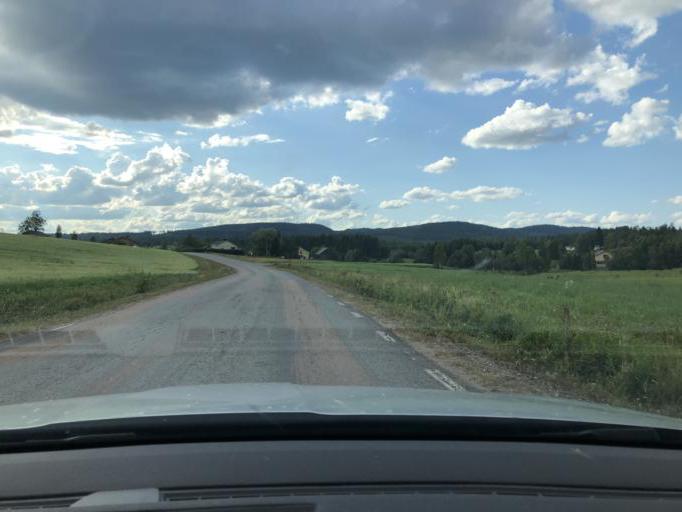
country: SE
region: Vaesternorrland
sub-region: Solleftea Kommun
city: Solleftea
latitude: 63.2054
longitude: 17.1355
